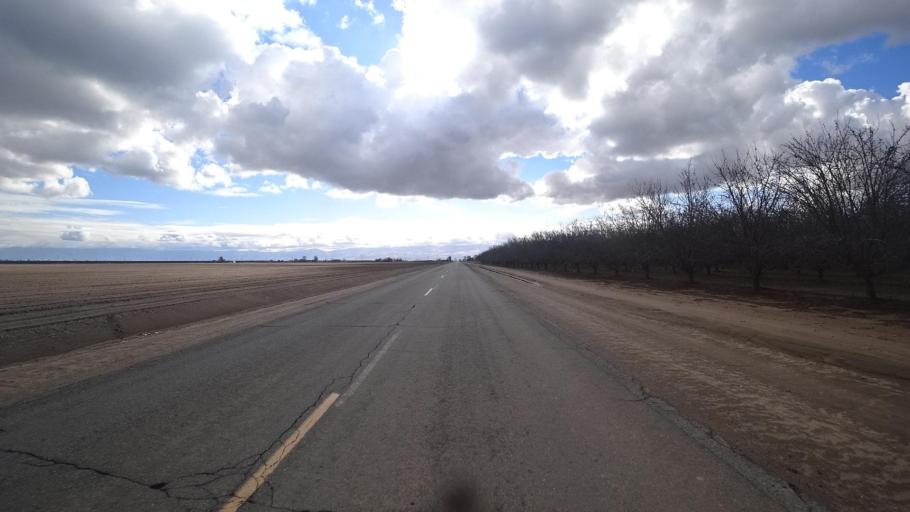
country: US
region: California
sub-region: Kern County
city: Greenfield
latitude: 35.2180
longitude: -119.0569
